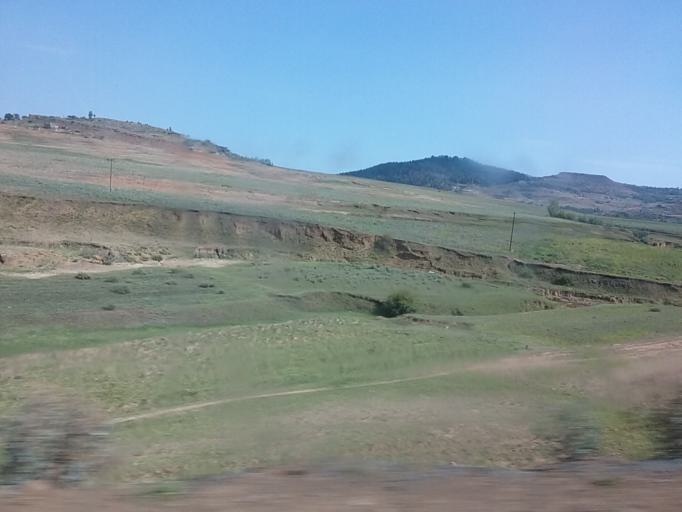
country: LS
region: Berea
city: Teyateyaneng
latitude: -29.0896
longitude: 27.9450
